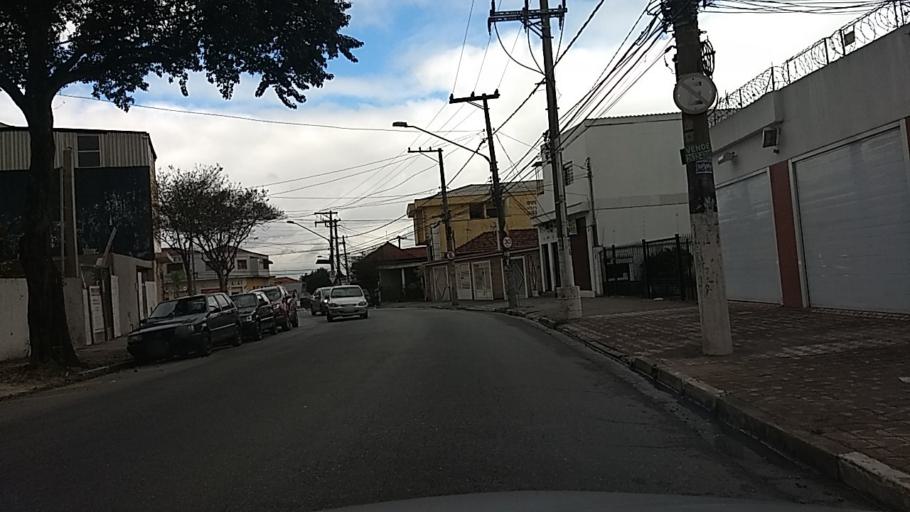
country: BR
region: Sao Paulo
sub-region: Sao Paulo
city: Sao Paulo
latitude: -23.5092
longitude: -46.5934
